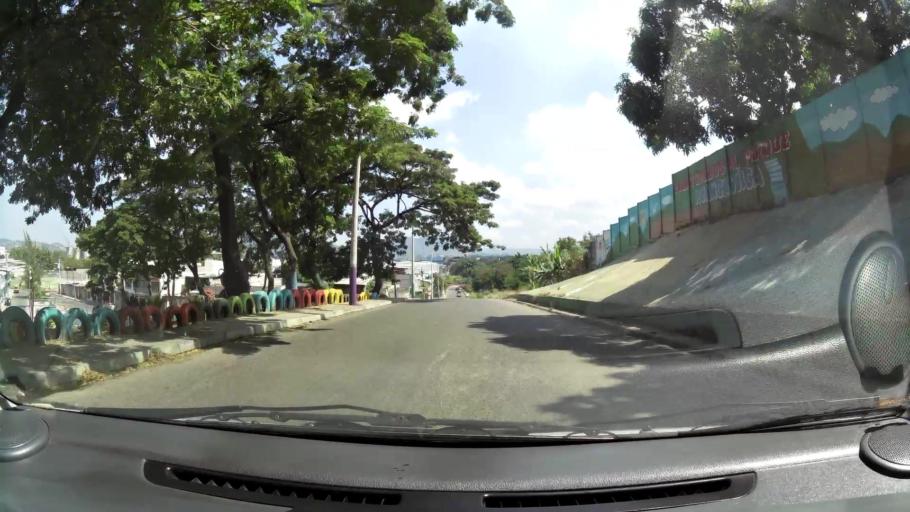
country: EC
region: Guayas
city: Guayaquil
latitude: -2.1183
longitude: -79.9265
